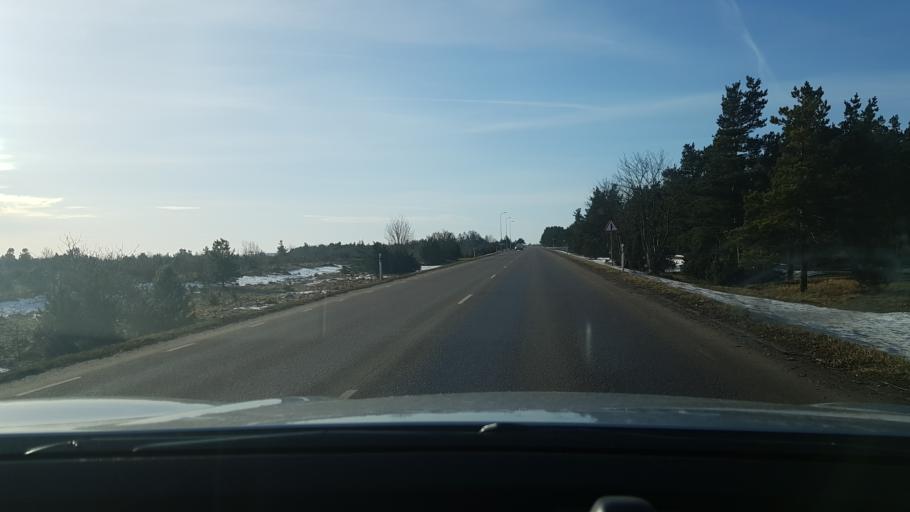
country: EE
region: Saare
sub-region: Kuressaare linn
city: Kuressaare
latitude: 58.2472
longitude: 22.5059
